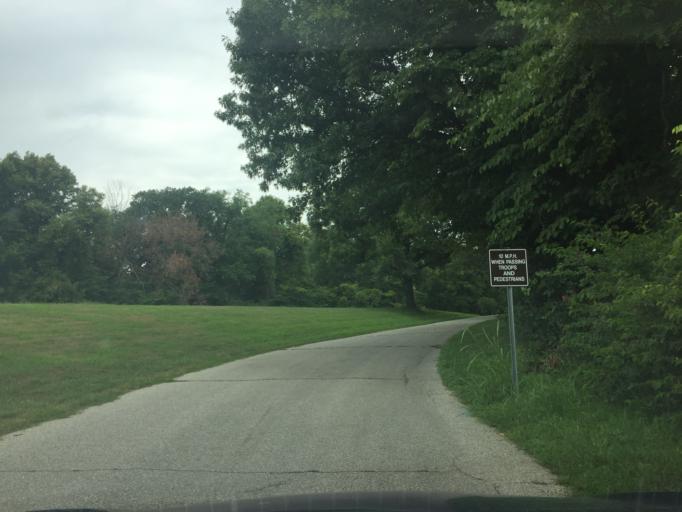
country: US
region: Missouri
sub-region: Platte County
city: Weston
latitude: 39.3694
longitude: -94.9223
